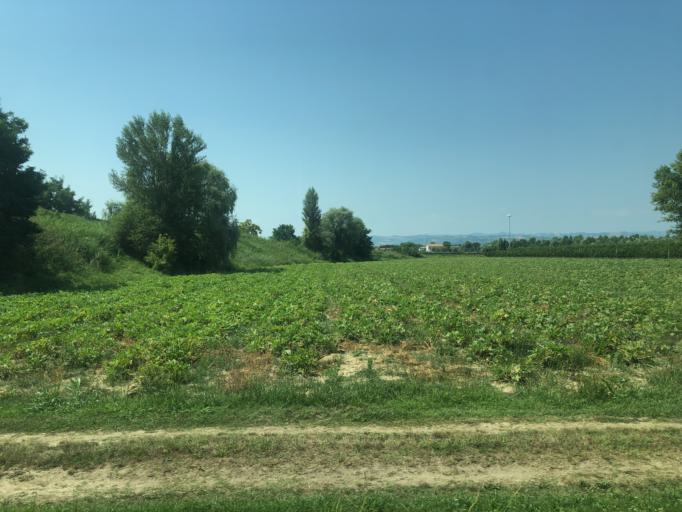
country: IT
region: Emilia-Romagna
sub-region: Forli-Cesena
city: Forlimpopoli
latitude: 44.2052
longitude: 12.1014
